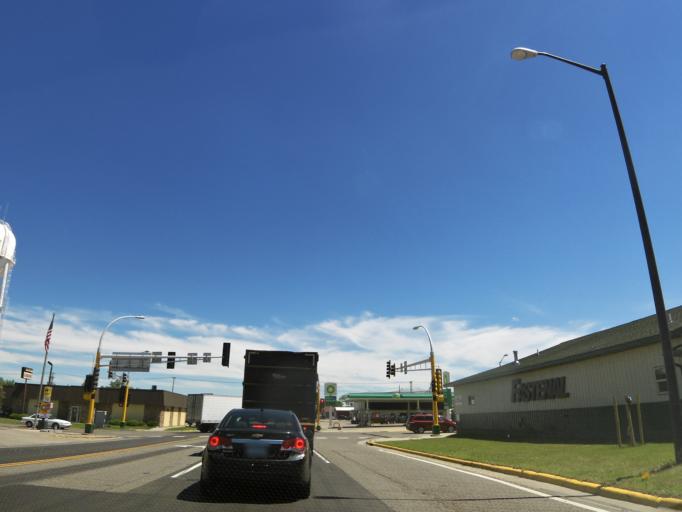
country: US
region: Minnesota
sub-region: Wadena County
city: Wadena
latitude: 46.4424
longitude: -95.1367
